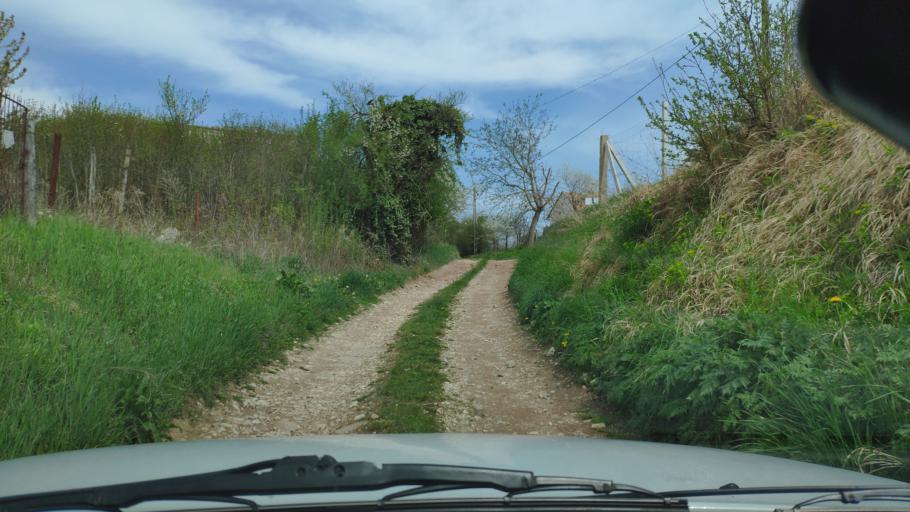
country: HU
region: Zala
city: Nagykanizsa
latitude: 46.4264
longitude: 17.0167
